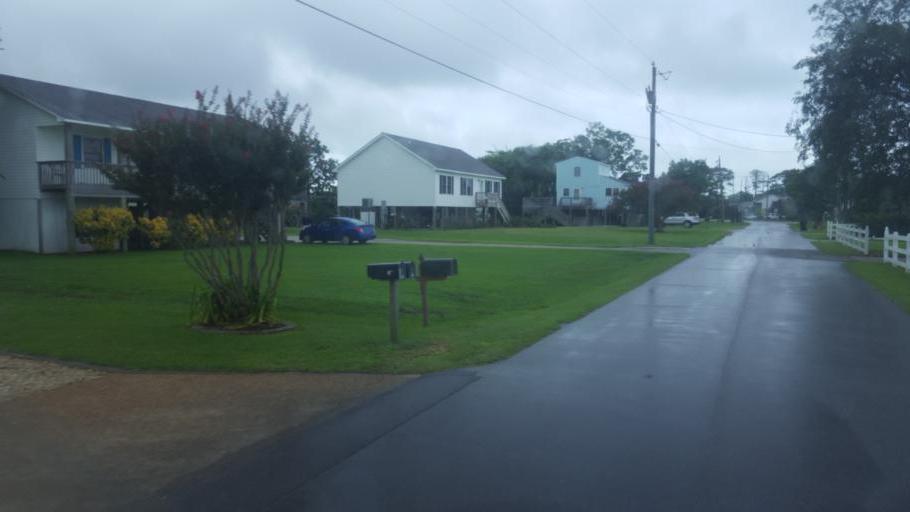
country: US
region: North Carolina
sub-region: Dare County
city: Wanchese
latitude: 35.8388
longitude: -75.6227
